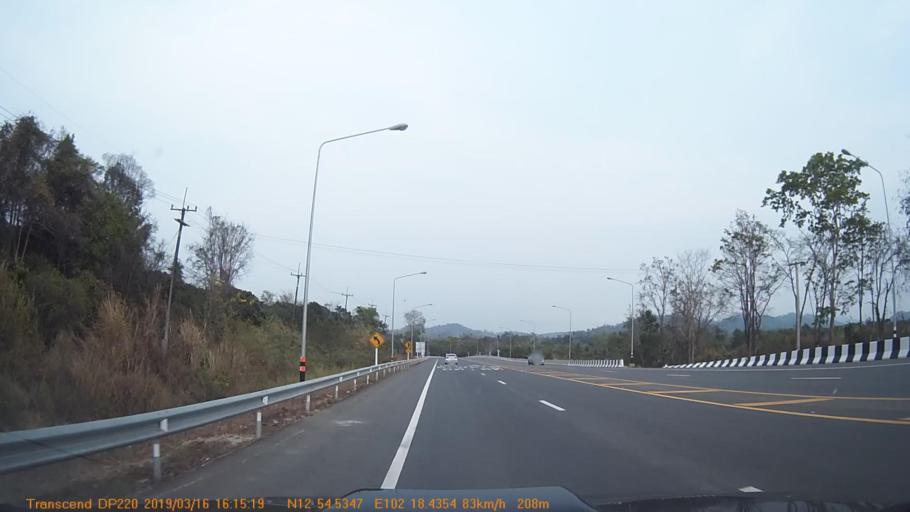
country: TH
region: Chanthaburi
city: Pong Nam Ron
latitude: 12.9088
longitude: 102.3074
